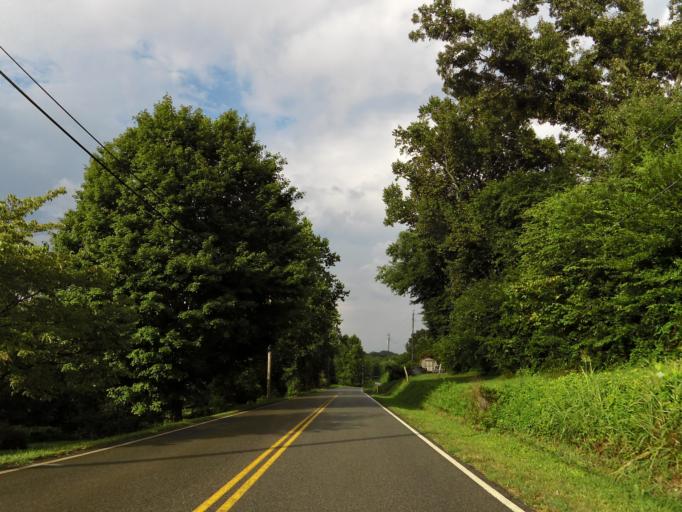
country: US
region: Tennessee
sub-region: Blount County
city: Wildwood
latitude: 35.8074
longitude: -83.8798
